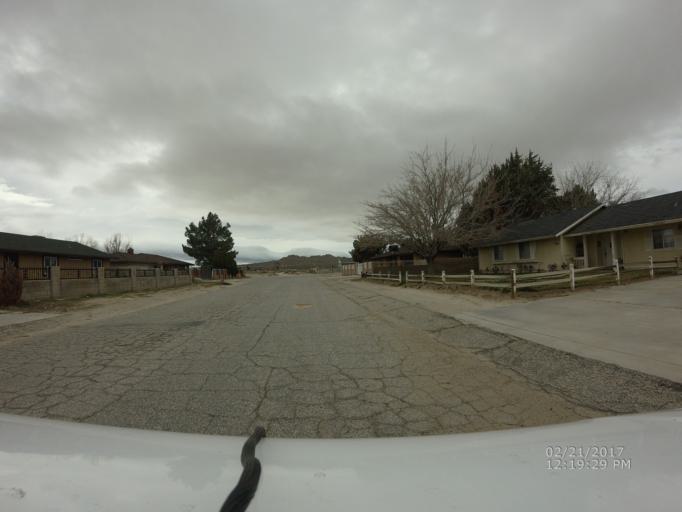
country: US
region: California
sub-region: Los Angeles County
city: Lake Los Angeles
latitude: 34.6325
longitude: -117.8605
